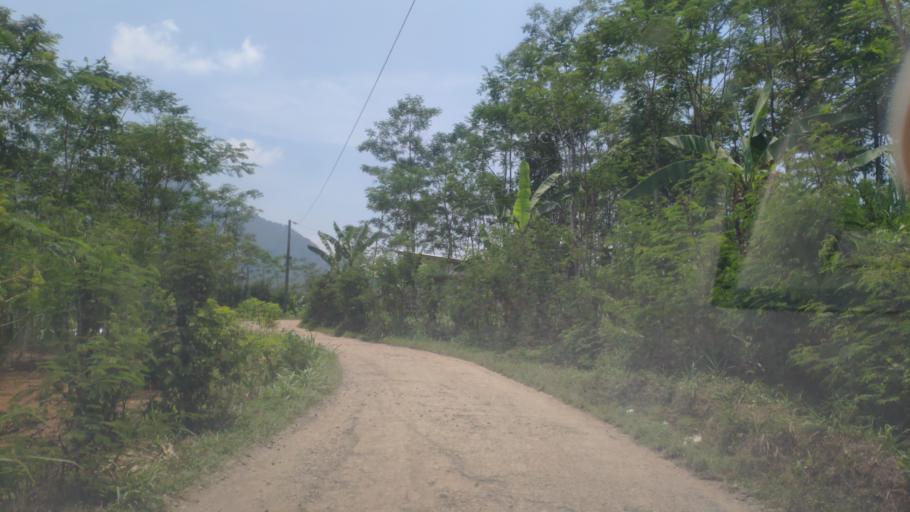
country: ID
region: Central Java
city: Wonosobo
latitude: -7.2838
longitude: 109.7360
